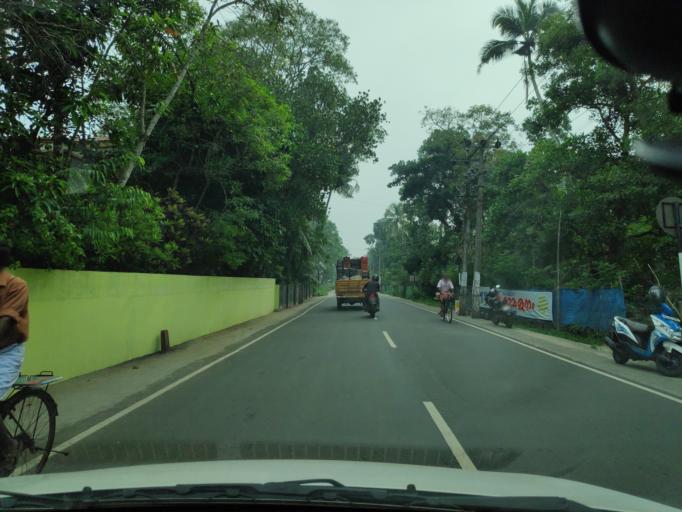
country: IN
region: Kerala
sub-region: Alappuzha
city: Shertallai
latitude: 9.6075
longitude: 76.3471
